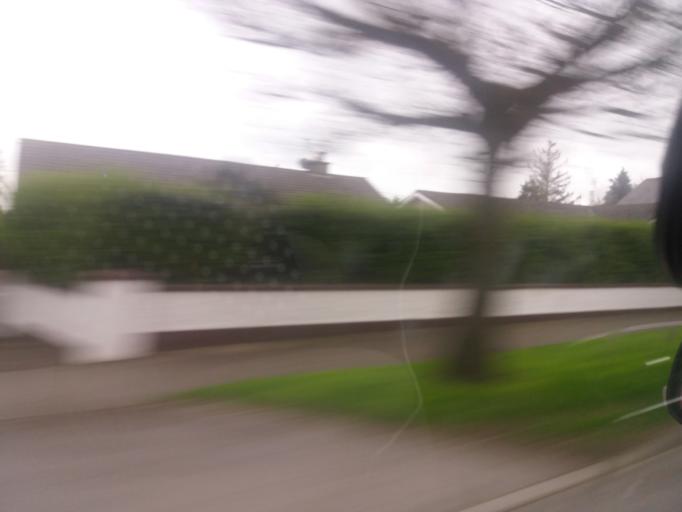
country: IE
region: Munster
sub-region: County Limerick
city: Adare
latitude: 52.5572
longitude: -8.7977
